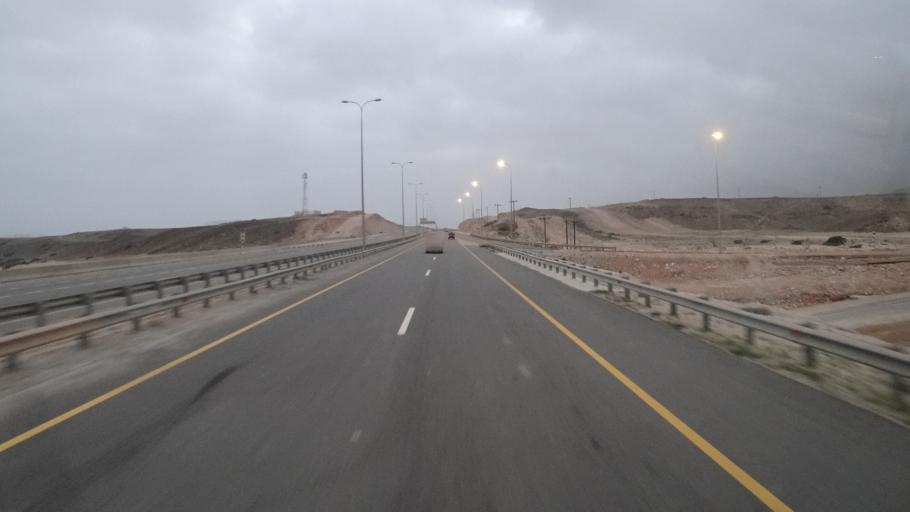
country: OM
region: Zufar
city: Salalah
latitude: 17.0497
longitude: 54.4676
